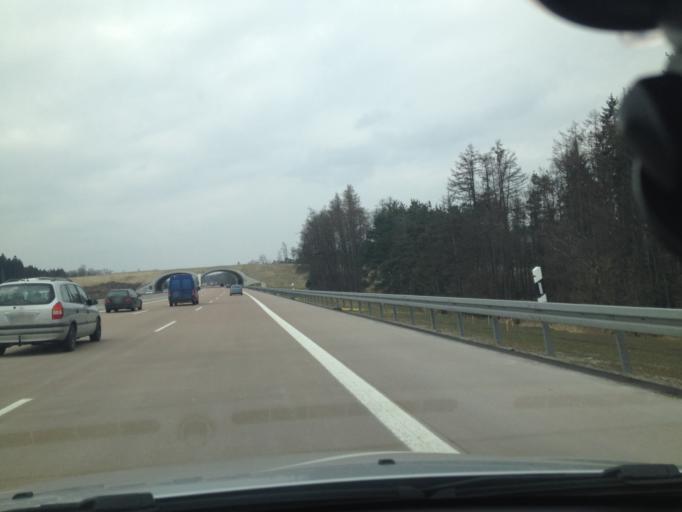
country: DE
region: Bavaria
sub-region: Swabia
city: Landensberg
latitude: 48.4043
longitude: 10.5263
